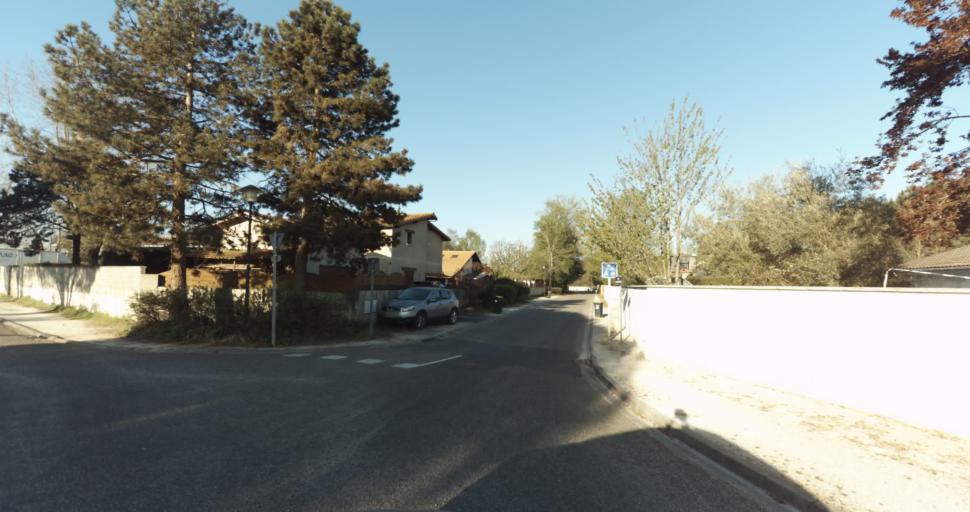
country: FR
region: Aquitaine
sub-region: Departement de la Gironde
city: Martignas-sur-Jalle
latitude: 44.8159
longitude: -0.7832
